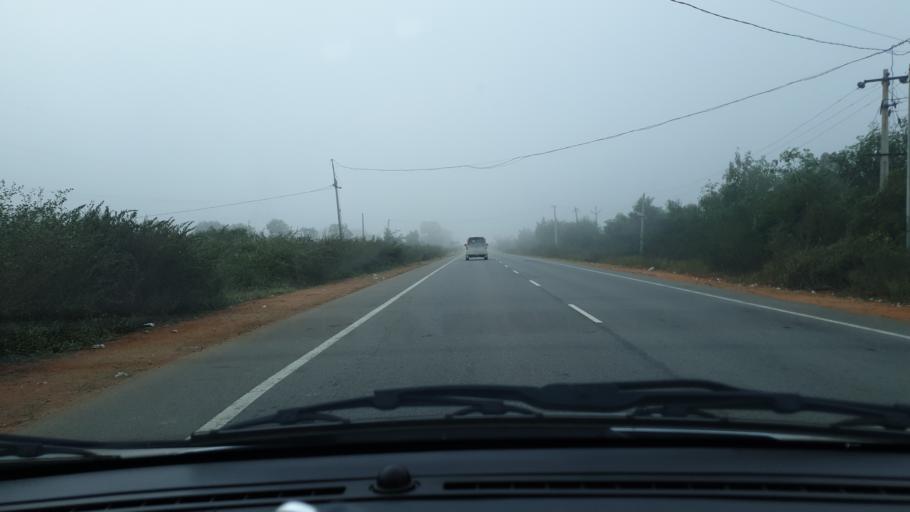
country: IN
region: Telangana
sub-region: Nalgonda
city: Devarkonda
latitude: 16.5999
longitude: 78.6807
